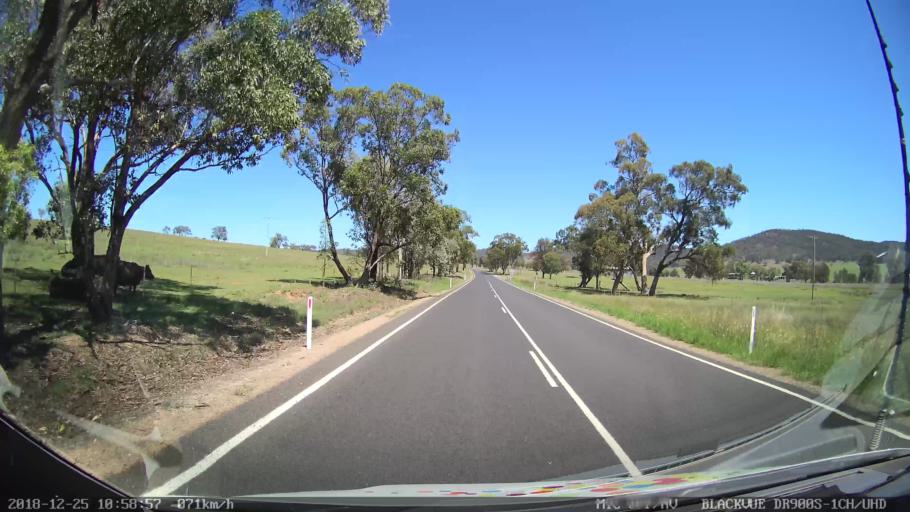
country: AU
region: New South Wales
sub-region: Upper Hunter Shire
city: Merriwa
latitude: -32.4046
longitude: 150.2342
